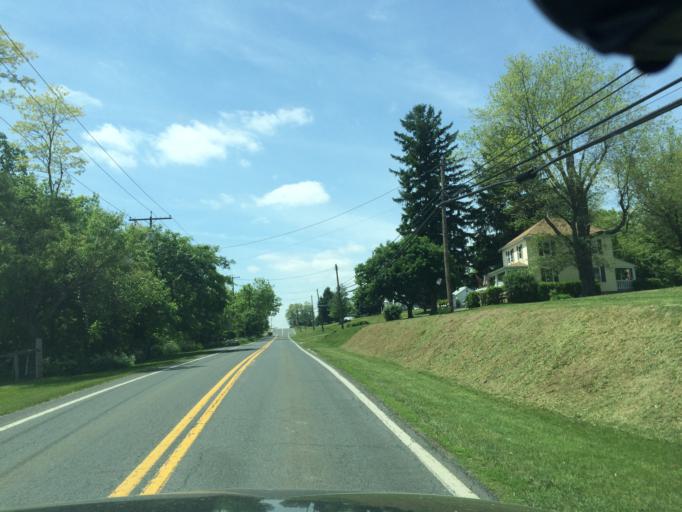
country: US
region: Maryland
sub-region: Carroll County
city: Westminster
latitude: 39.5462
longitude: -76.9420
